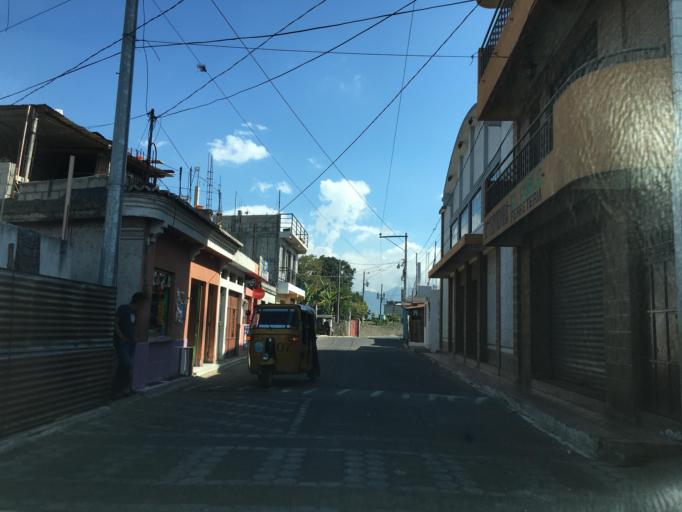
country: GT
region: Solola
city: San Antonio Palopo
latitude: 14.6667
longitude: -91.1654
